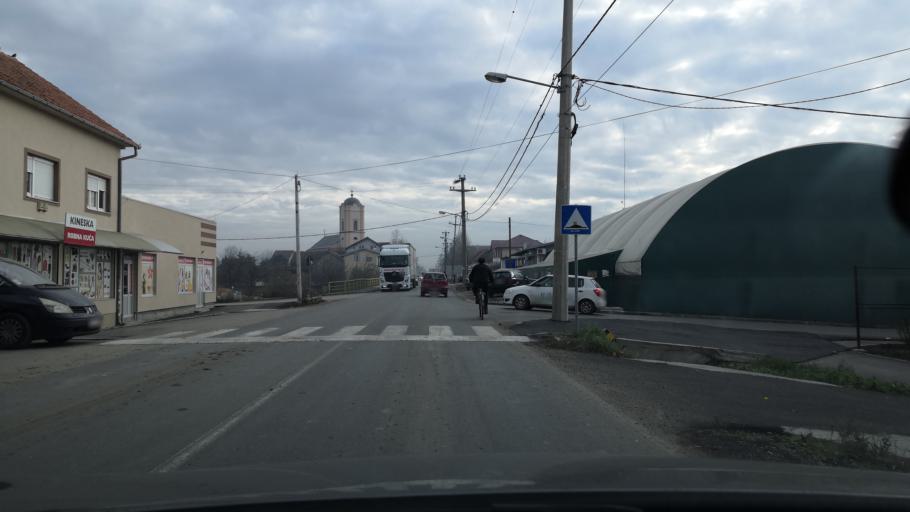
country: RS
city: Ugrinovci
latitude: 44.8763
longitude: 20.1848
